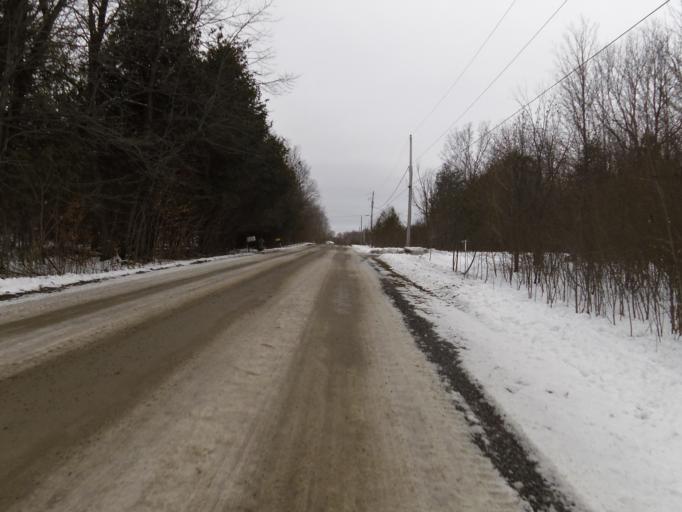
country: CA
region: Ontario
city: Carleton Place
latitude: 45.1391
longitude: -76.2510
